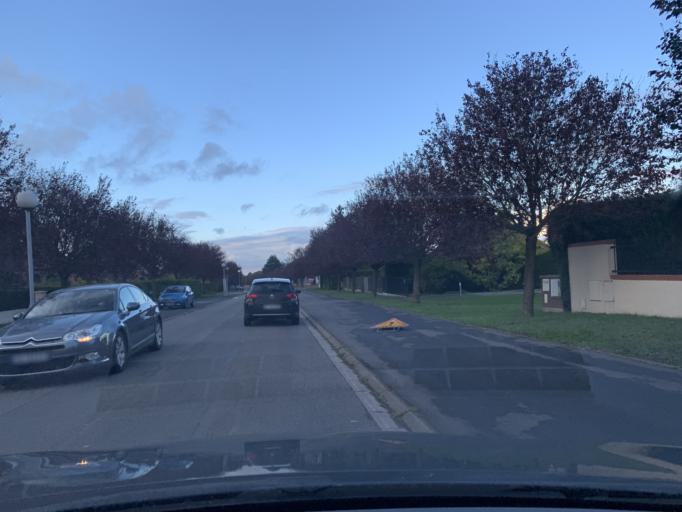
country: FR
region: Nord-Pas-de-Calais
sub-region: Departement du Nord
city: Proville
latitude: 50.1544
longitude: 3.2109
